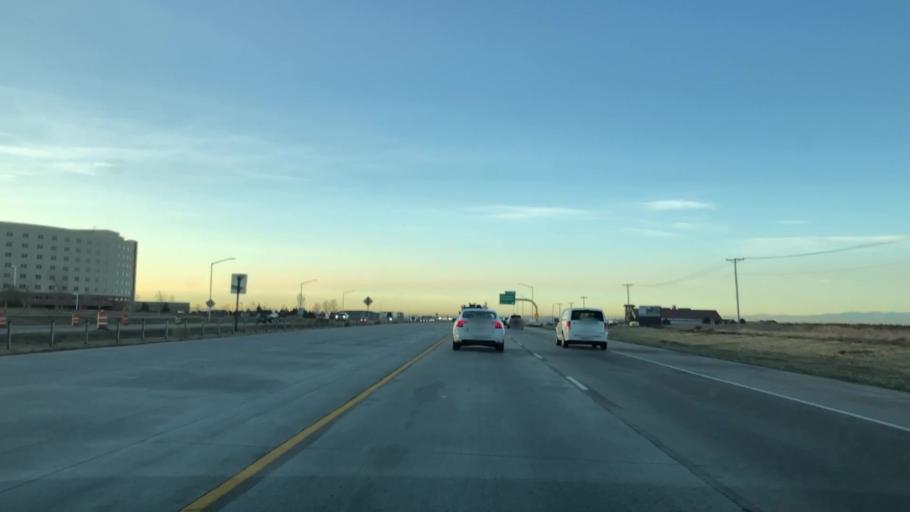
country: US
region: Colorado
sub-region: Larimer County
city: Loveland
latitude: 40.4430
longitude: -104.9929
